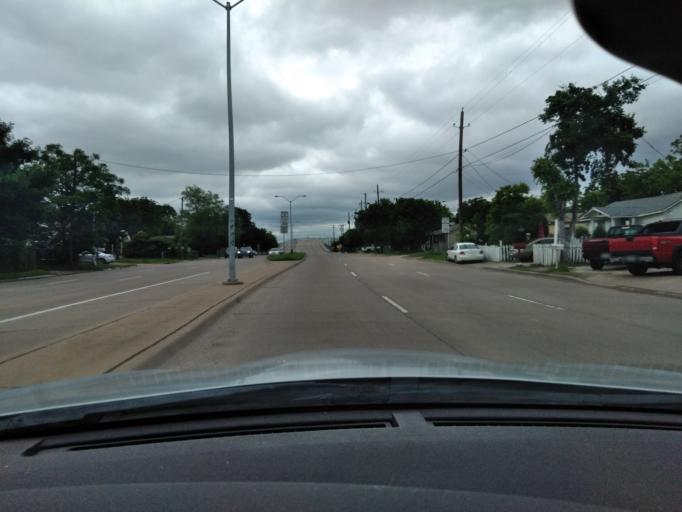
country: US
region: Texas
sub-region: Dallas County
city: Dallas
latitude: 32.7822
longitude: -96.8358
